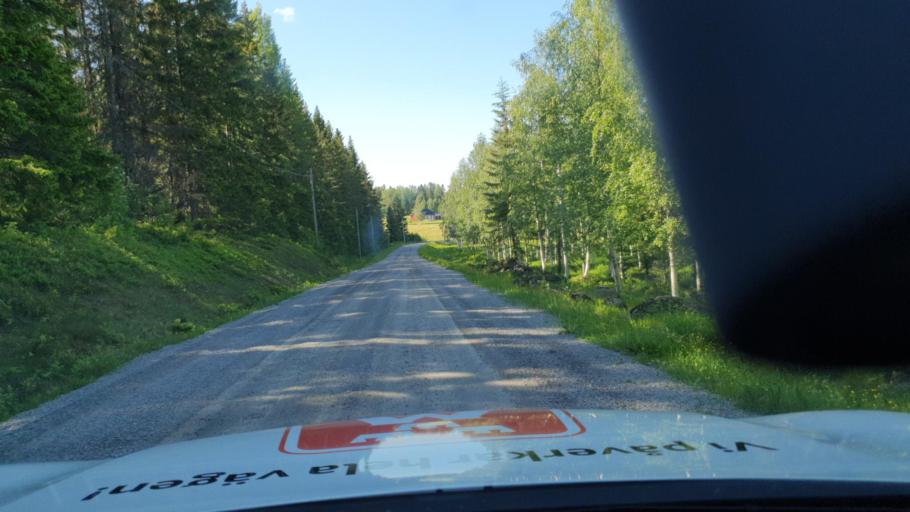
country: SE
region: Vaesterbotten
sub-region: Vannas Kommun
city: Vaennaes
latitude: 63.8123
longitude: 19.6330
